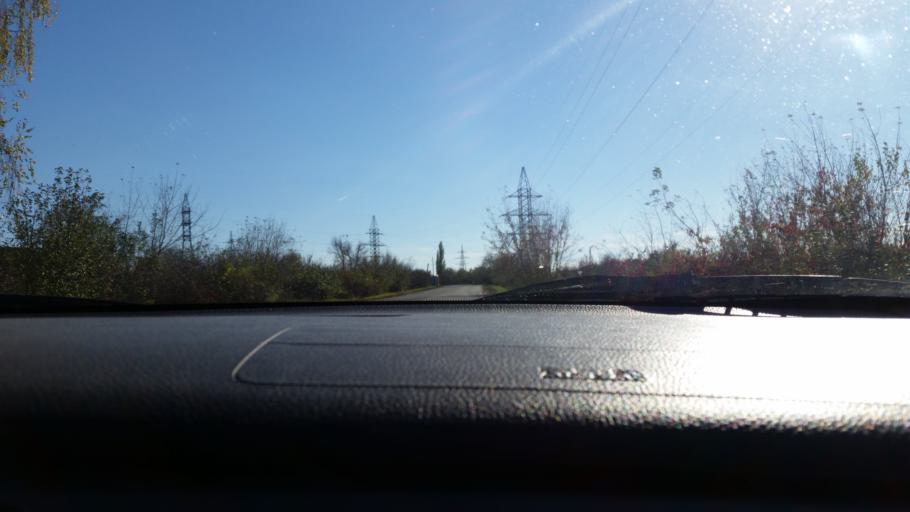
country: RU
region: Lipetsk
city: Gryazi
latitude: 52.4673
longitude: 39.9577
